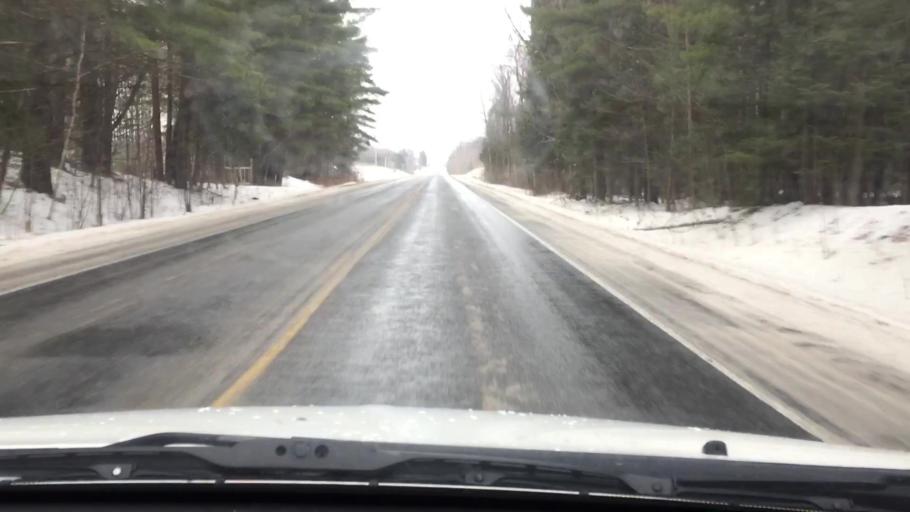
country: US
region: Michigan
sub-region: Osceola County
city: Reed City
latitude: 44.0540
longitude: -85.4439
